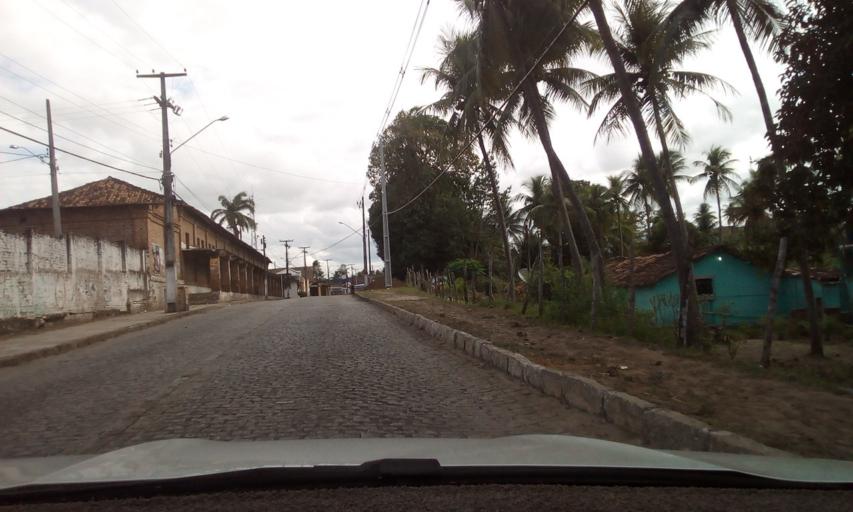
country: BR
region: Paraiba
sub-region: Rio Tinto
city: Rio Tinto
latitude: -6.8053
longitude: -35.0761
